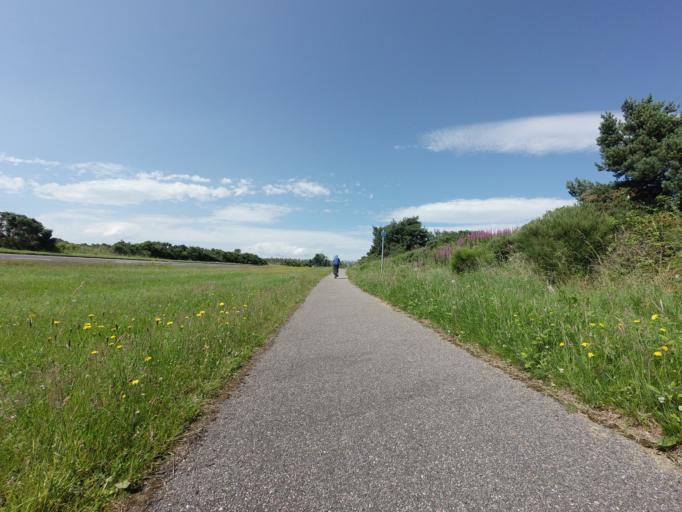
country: GB
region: Scotland
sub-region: Highland
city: Conon Bridge
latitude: 57.5385
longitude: -4.3666
